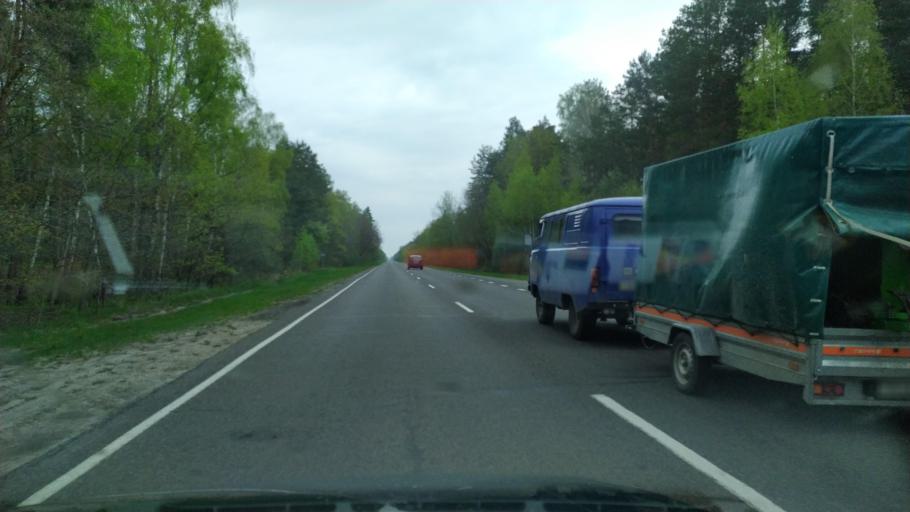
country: BY
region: Brest
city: Horad Kobryn
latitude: 52.3012
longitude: 24.5211
